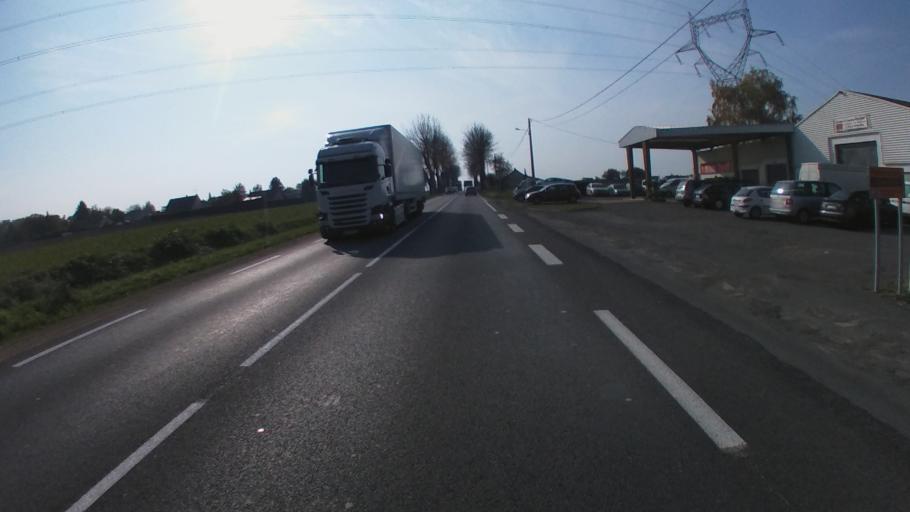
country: FR
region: Pays de la Loire
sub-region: Departement de Maine-et-Loire
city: Distre
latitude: 47.1993
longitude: -0.1237
